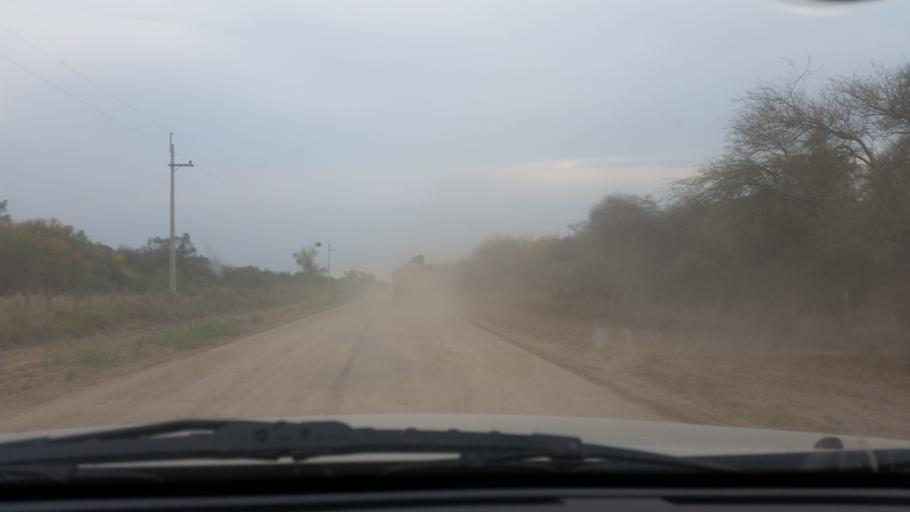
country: PY
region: Boqueron
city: Colonia Menno
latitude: -22.3506
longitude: -59.5710
